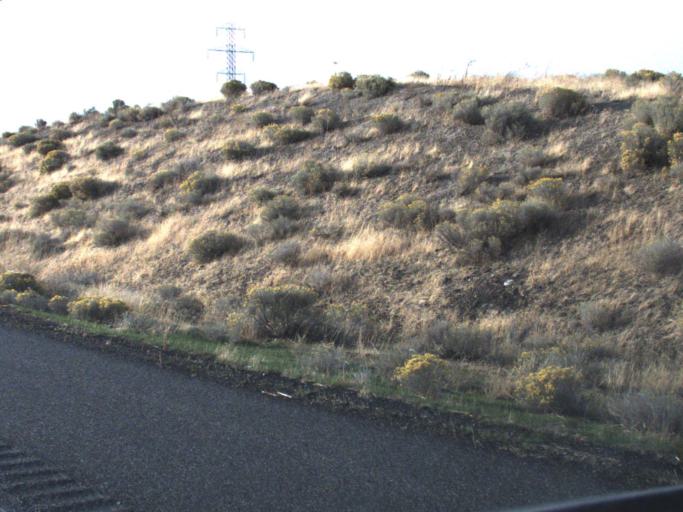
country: US
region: Washington
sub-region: Franklin County
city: West Pasco
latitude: 46.1756
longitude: -119.2257
